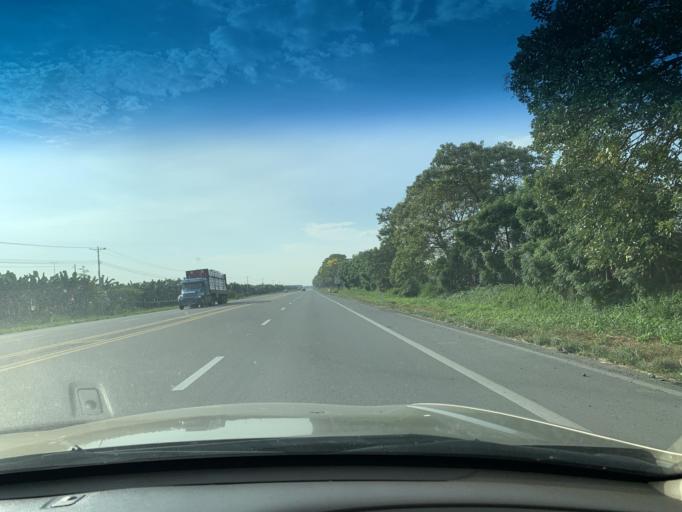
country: EC
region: Guayas
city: Coronel Marcelino Mariduena
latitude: -2.2774
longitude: -79.5329
